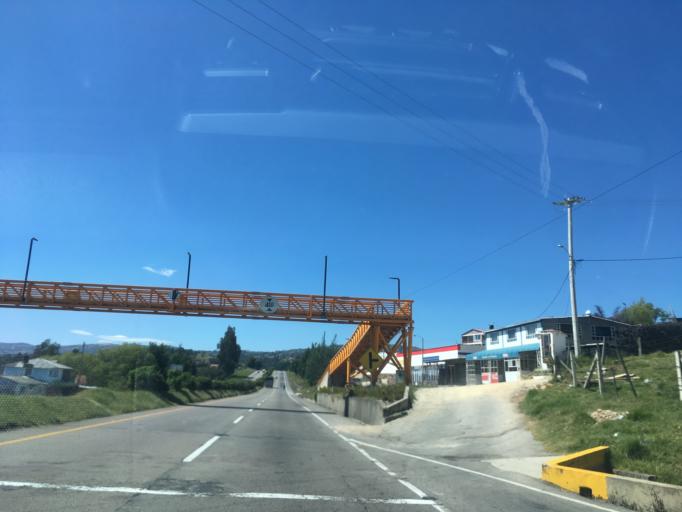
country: CO
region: Boyaca
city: Tuta
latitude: 5.6898
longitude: -73.2553
